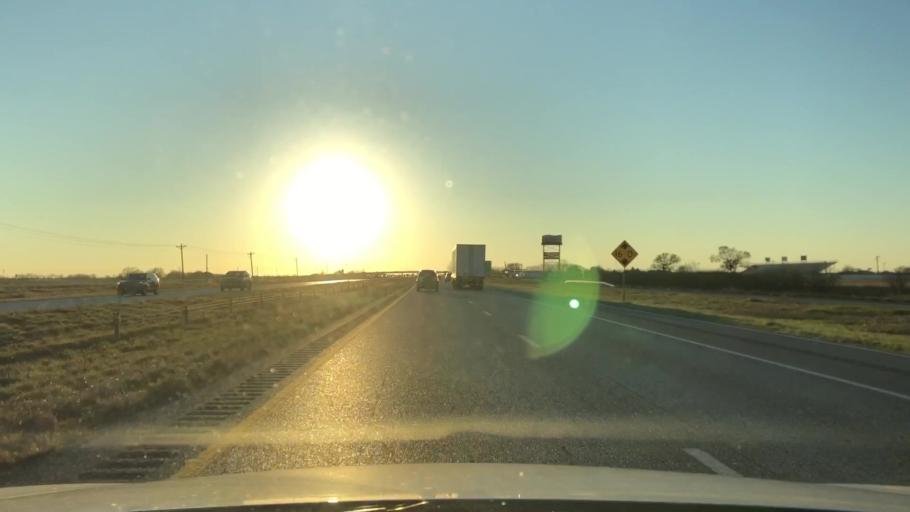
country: US
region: Texas
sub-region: Guadalupe County
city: Marion
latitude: 29.5227
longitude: -98.1300
